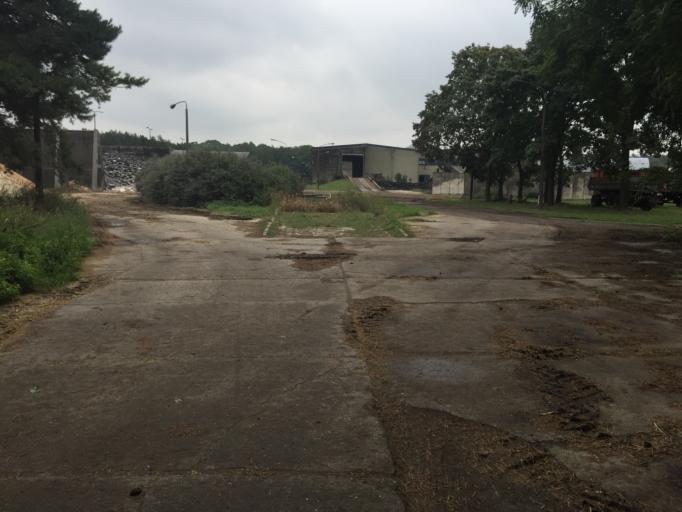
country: DE
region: Brandenburg
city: Rangsdorf
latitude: 52.3184
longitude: 13.3823
